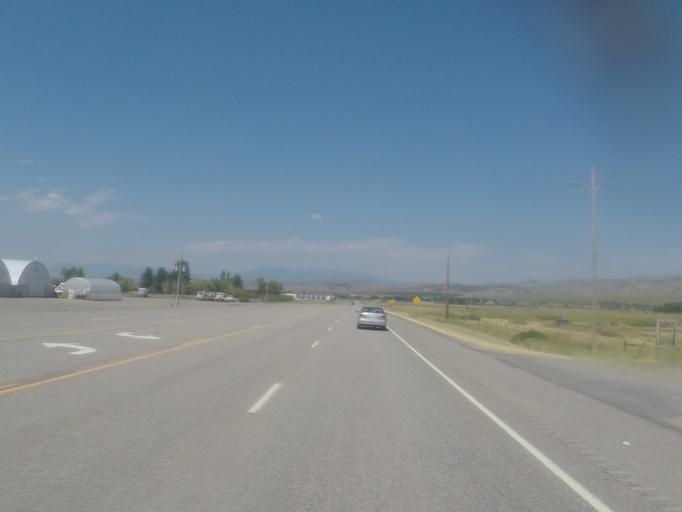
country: US
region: Montana
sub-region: Broadwater County
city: Townsend
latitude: 46.1575
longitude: -111.4606
